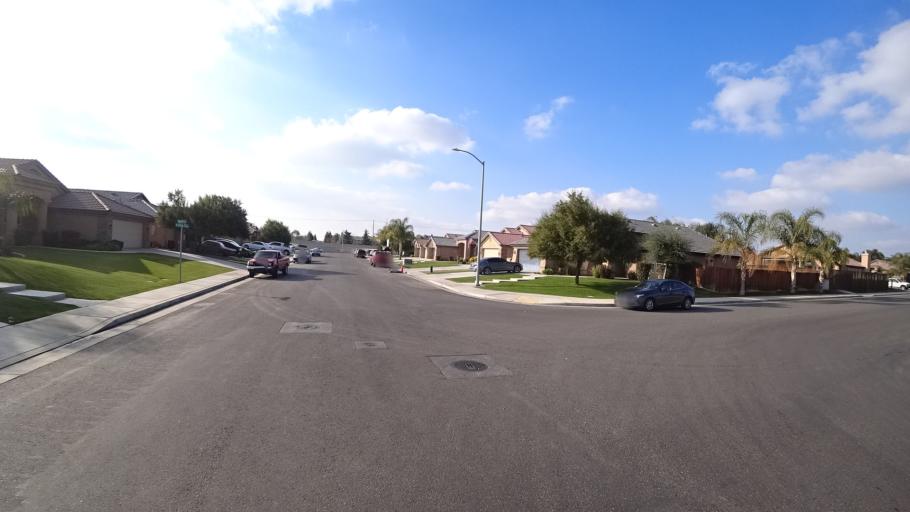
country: US
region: California
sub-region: Kern County
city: Greenacres
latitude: 35.3075
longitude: -119.1078
